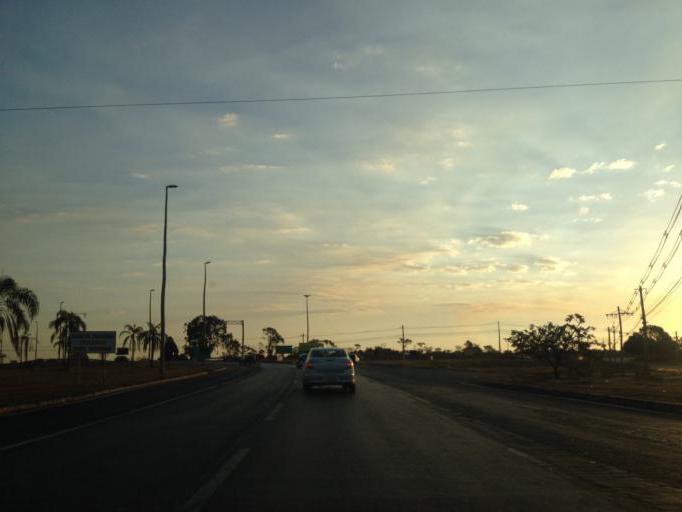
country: BR
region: Federal District
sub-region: Brasilia
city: Brasilia
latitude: -15.6872
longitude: -47.8594
